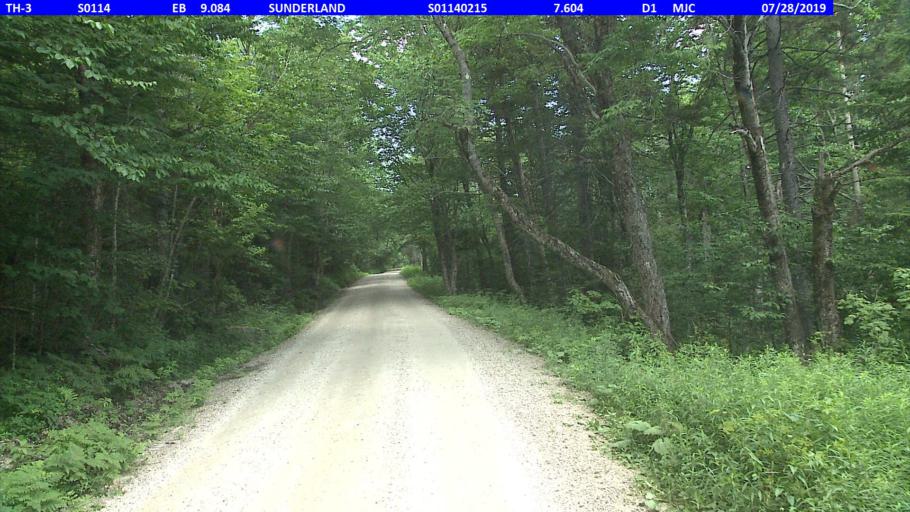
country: US
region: Vermont
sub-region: Bennington County
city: Arlington
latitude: 43.0522
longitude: -73.0374
